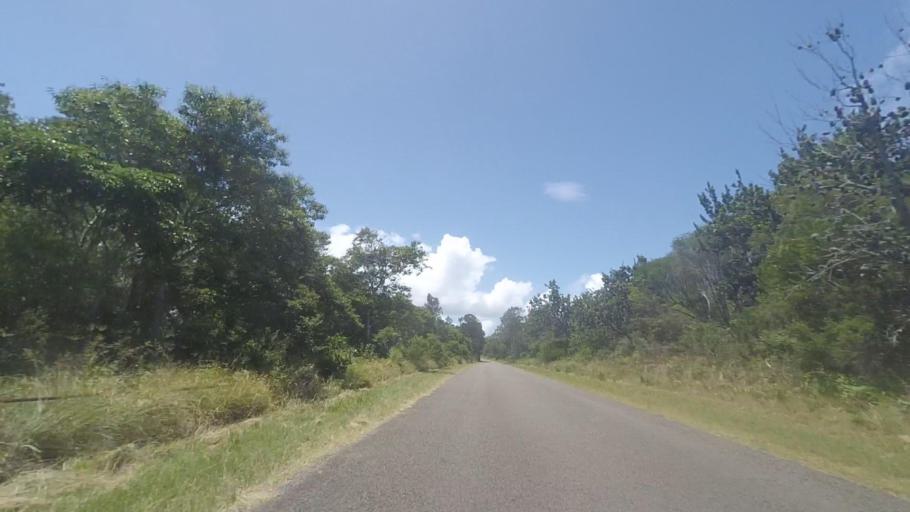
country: AU
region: New South Wales
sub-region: Great Lakes
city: Bulahdelah
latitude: -32.5362
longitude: 152.3196
